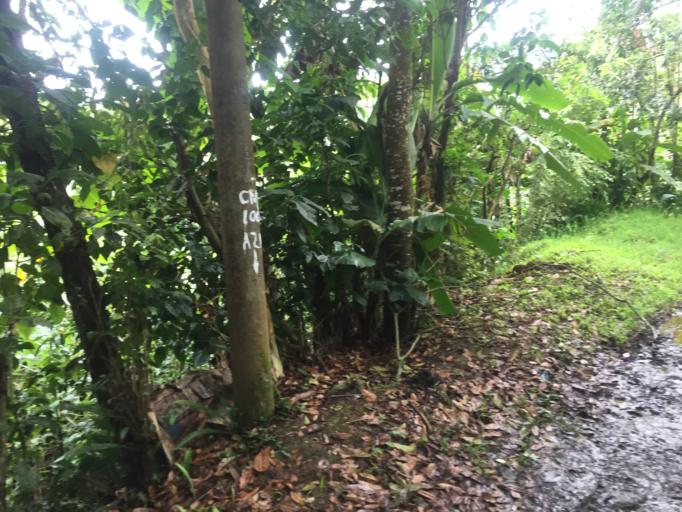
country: CO
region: Valle del Cauca
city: Cali
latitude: 3.4619
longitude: -76.6354
